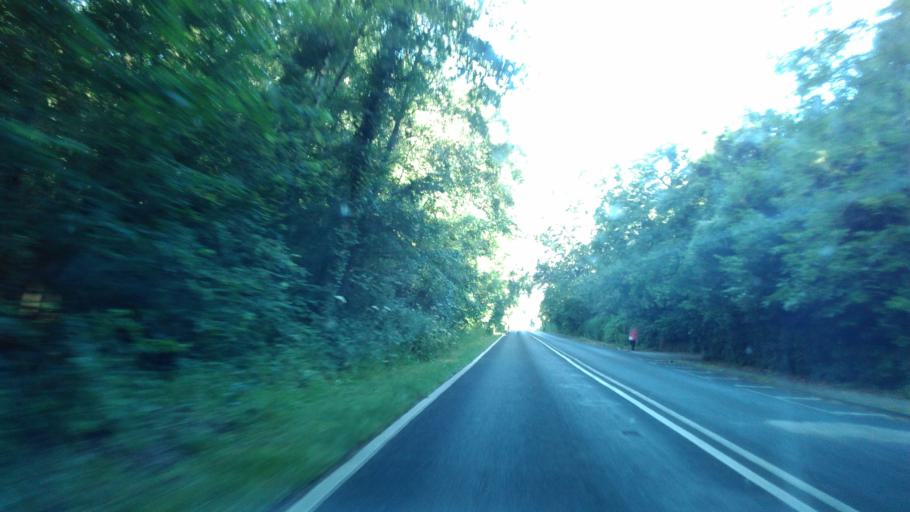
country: GB
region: England
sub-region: Kent
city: Dunkirk
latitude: 51.2924
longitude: 0.9711
